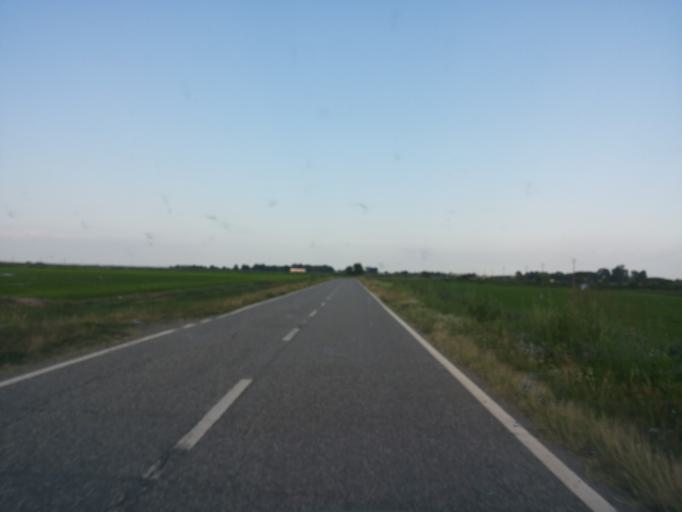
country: IT
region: Piedmont
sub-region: Provincia di Vercelli
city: Stroppiana
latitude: 45.2629
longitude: 8.4471
